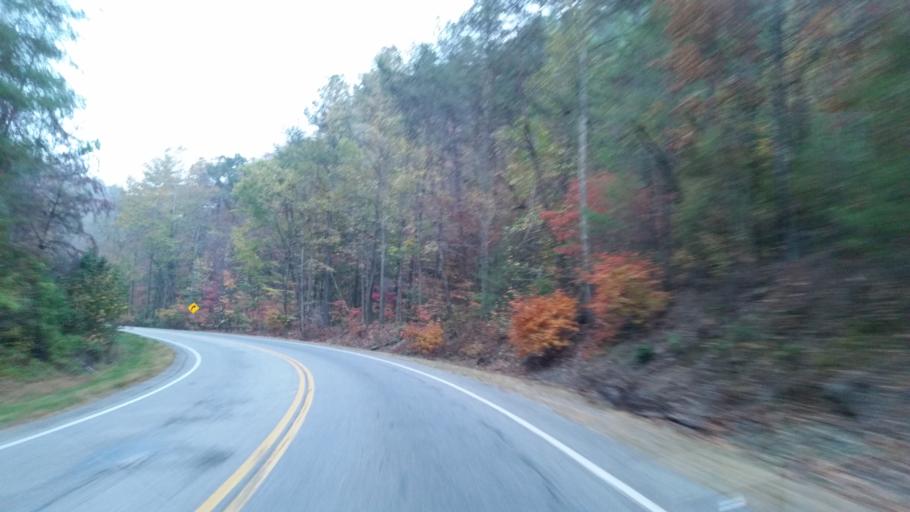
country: US
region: Georgia
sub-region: Gilmer County
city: Ellijay
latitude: 34.5825
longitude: -84.6541
